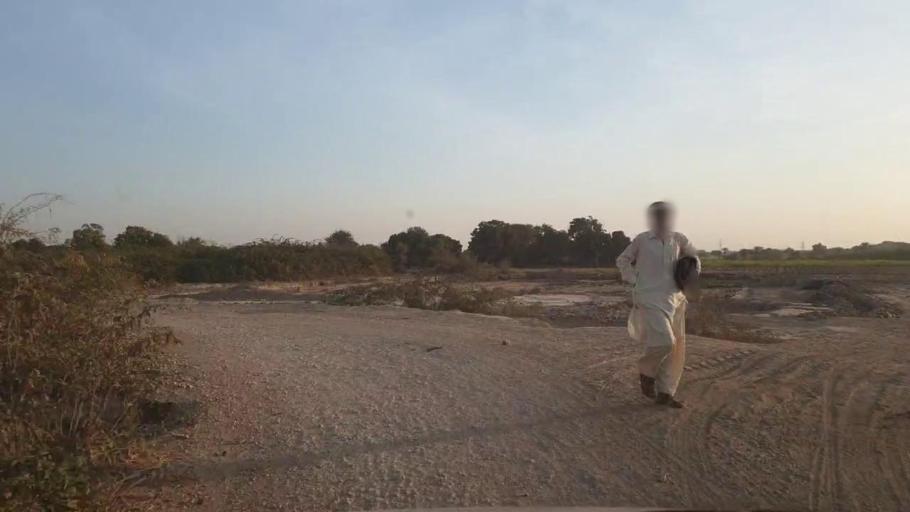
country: PK
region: Sindh
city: Chambar
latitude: 25.2857
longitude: 68.8184
